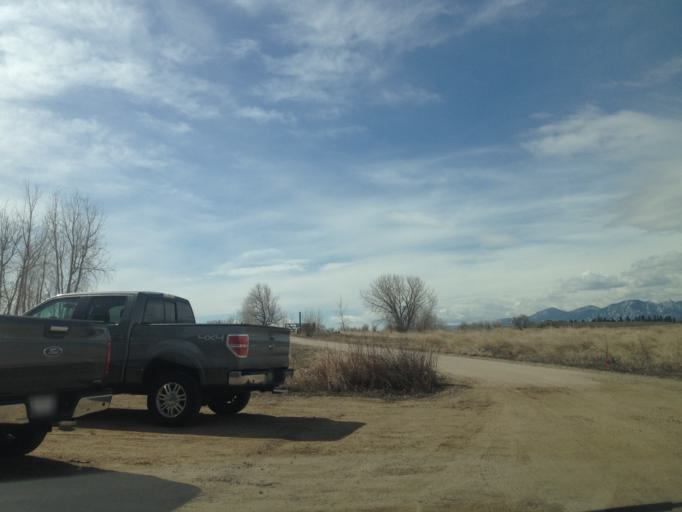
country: US
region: Colorado
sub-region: Boulder County
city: Gunbarrel
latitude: 40.0239
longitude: -105.1830
